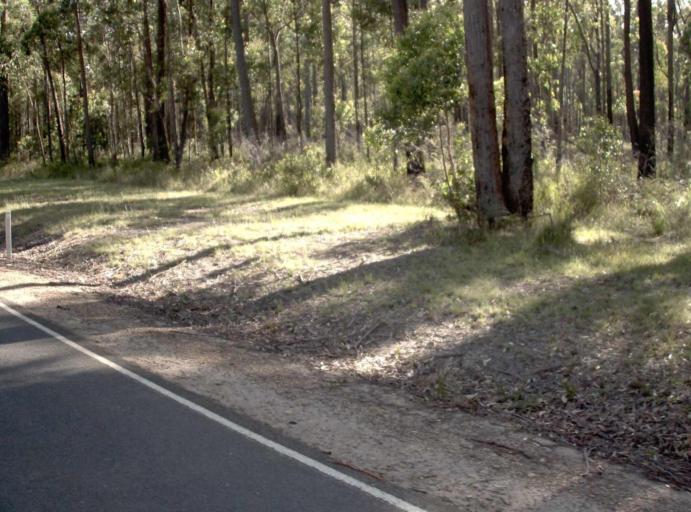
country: AU
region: Victoria
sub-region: East Gippsland
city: Lakes Entrance
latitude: -37.6744
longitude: 148.4726
